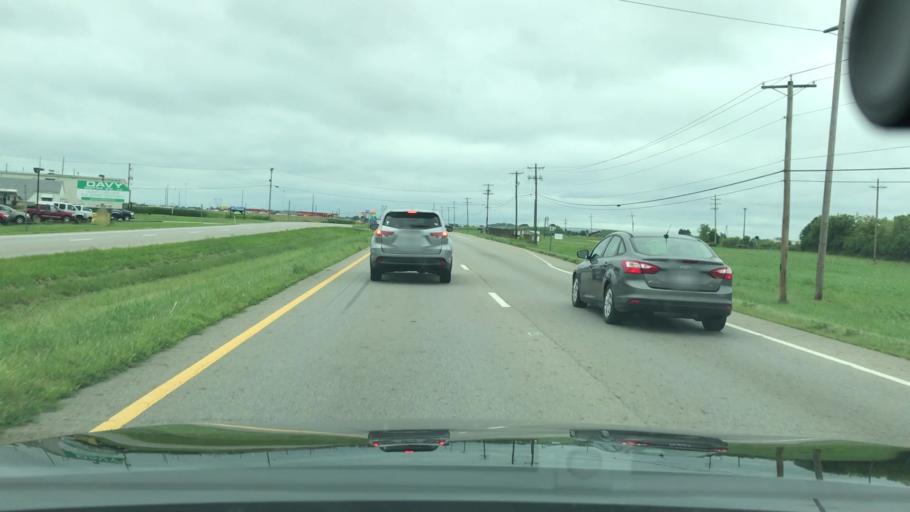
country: US
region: Ohio
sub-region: Pickaway County
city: Logan Elm Village
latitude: 39.5639
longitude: -82.9562
